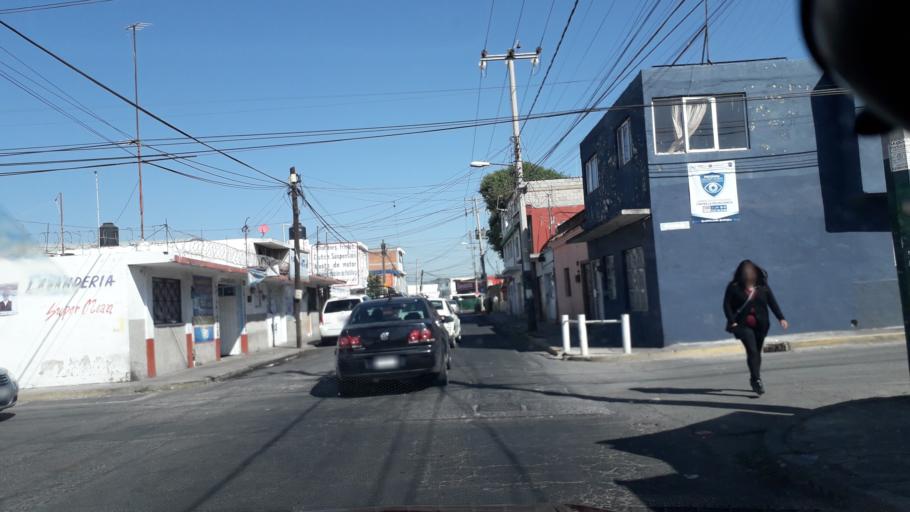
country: MX
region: Puebla
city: Puebla
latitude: 19.0718
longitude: -98.2101
